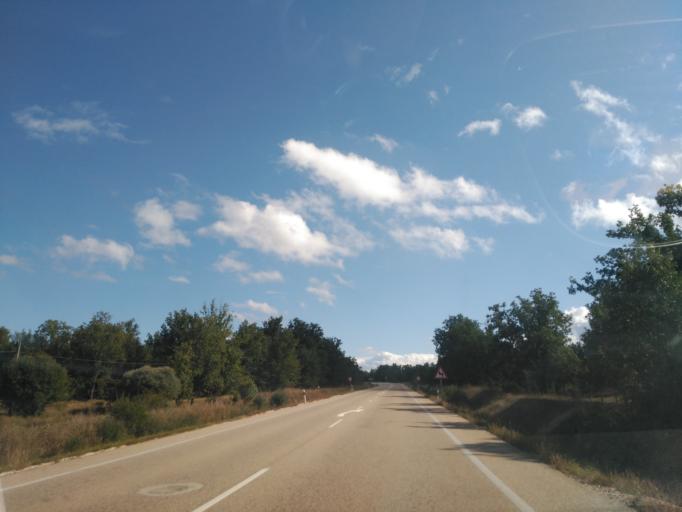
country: ES
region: Castille and Leon
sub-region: Provincia de Burgos
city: Pinilla de los Barruecos
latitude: 41.9315
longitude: -3.2829
